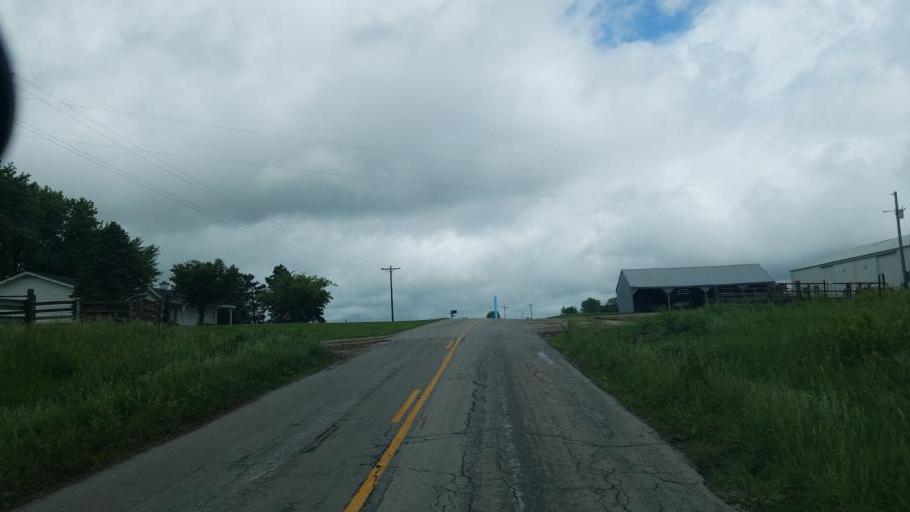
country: US
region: Missouri
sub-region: Mercer County
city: Princeton
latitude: 40.3703
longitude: -93.6805
